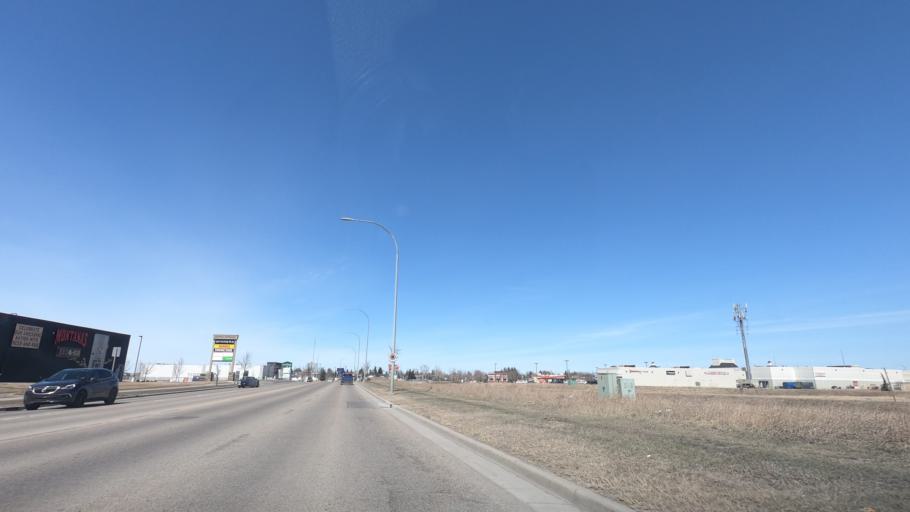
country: CA
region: Alberta
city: Airdrie
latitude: 51.2668
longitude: -114.0072
